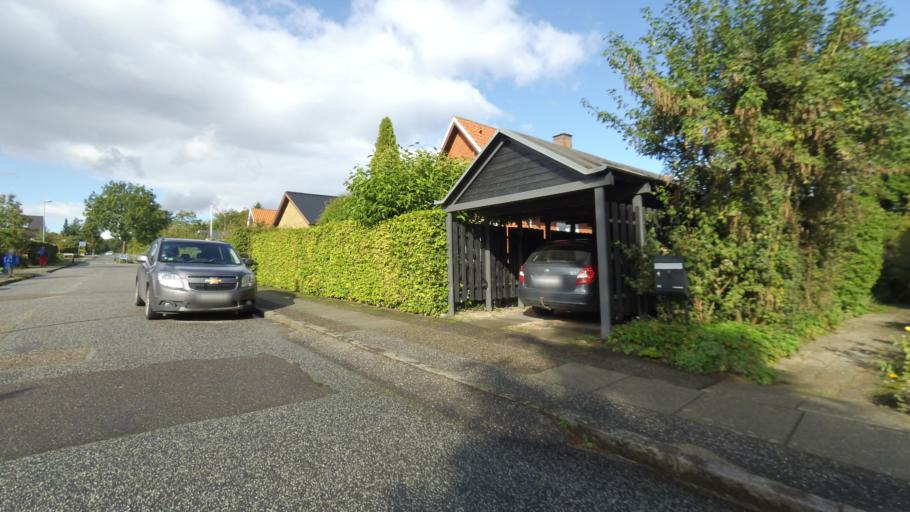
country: DK
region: Central Jutland
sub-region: Arhus Kommune
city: Stavtrup
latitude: 56.1574
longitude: 10.1603
